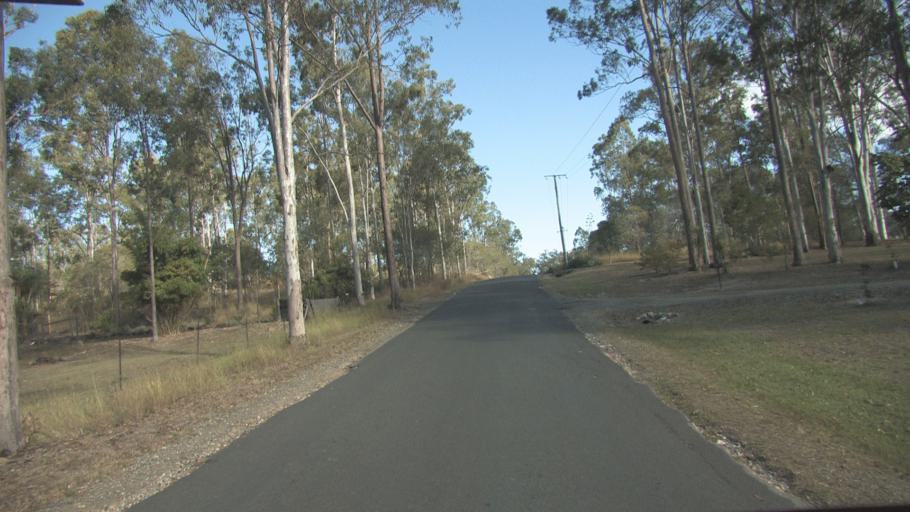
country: AU
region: Queensland
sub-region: Logan
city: Cedar Vale
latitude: -27.8325
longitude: 153.0612
